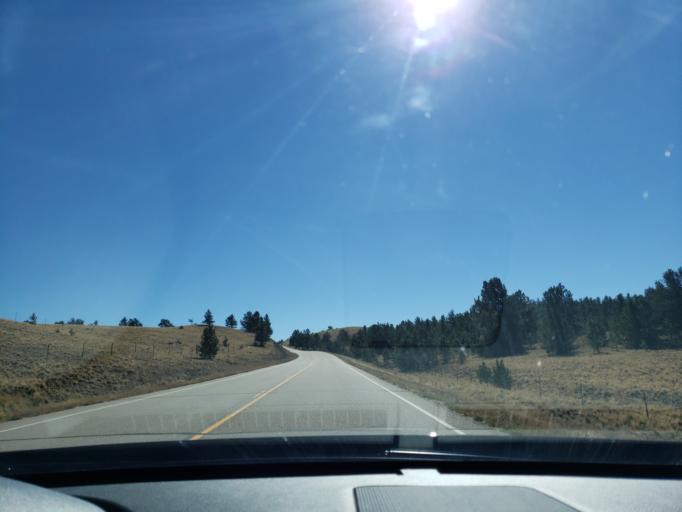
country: US
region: Colorado
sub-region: Chaffee County
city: Buena Vista
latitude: 38.8956
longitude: -105.6909
